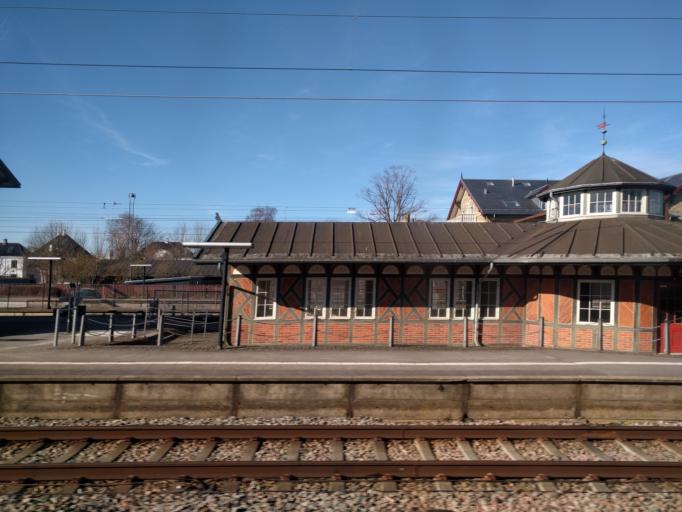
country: DK
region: Capital Region
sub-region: Gentofte Kommune
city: Charlottenlund
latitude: 55.7748
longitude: 12.5876
